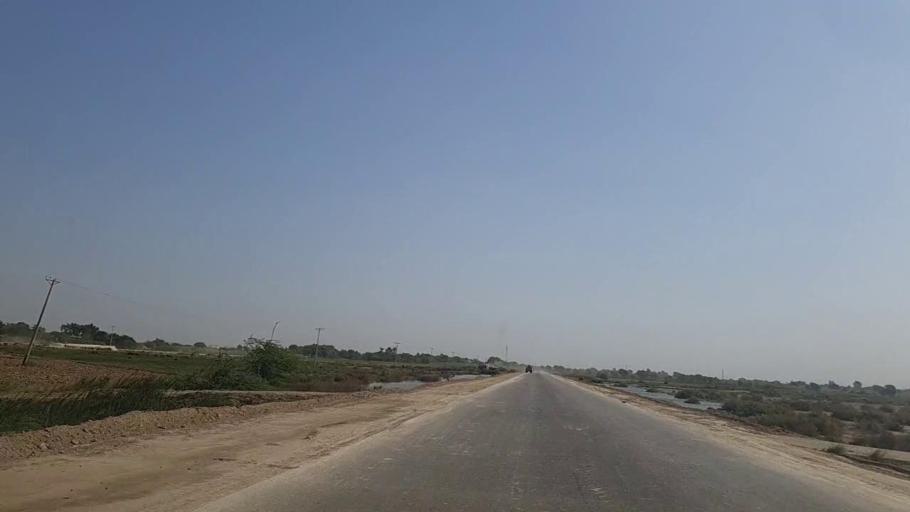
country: PK
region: Sindh
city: Mirpur Batoro
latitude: 24.7475
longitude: 68.2399
